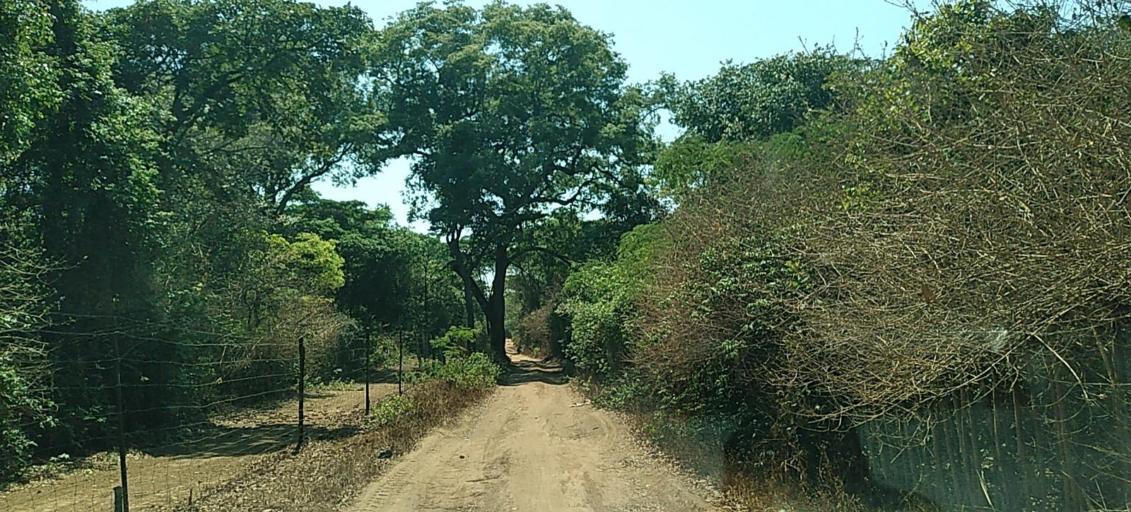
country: ZM
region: Copperbelt
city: Luanshya
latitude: -13.0085
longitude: 28.4549
